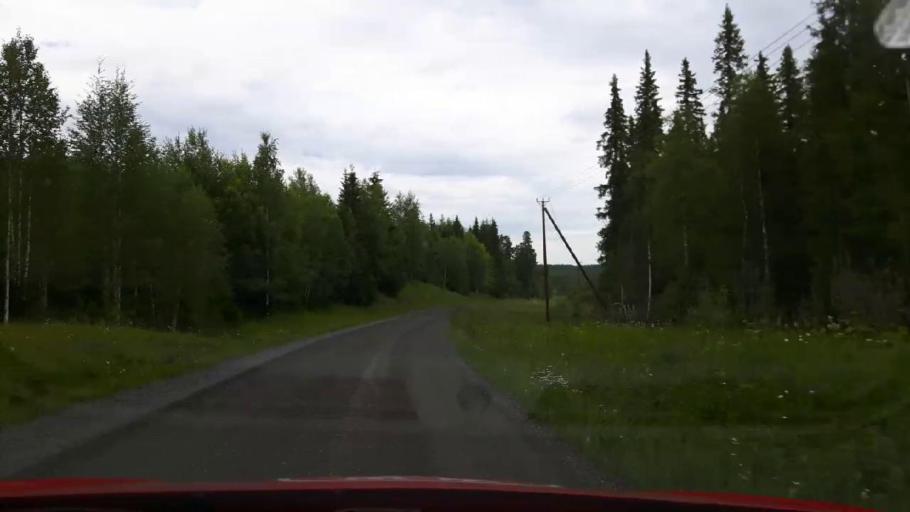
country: SE
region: Jaemtland
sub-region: Stroemsunds Kommun
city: Stroemsund
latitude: 63.4698
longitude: 15.2870
